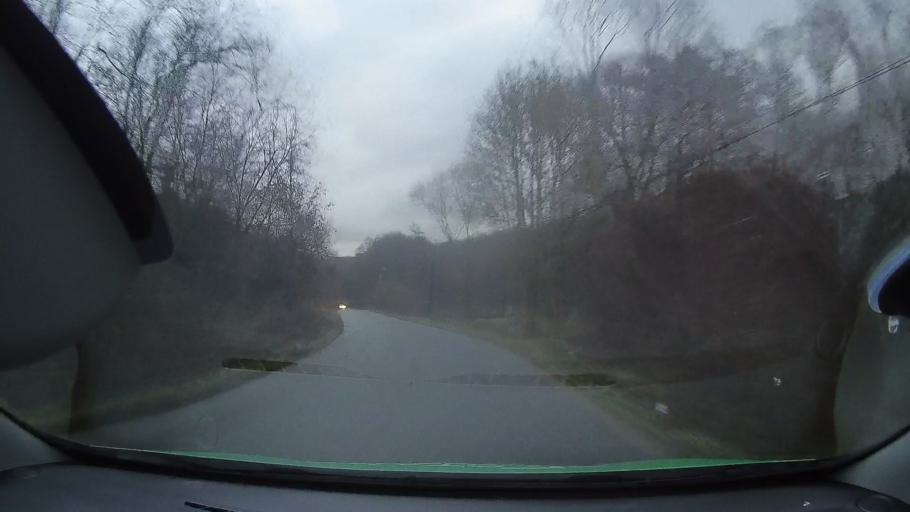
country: RO
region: Hunedoara
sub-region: Comuna Baia de Cris
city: Baia de Cris
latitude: 46.1947
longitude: 22.7176
